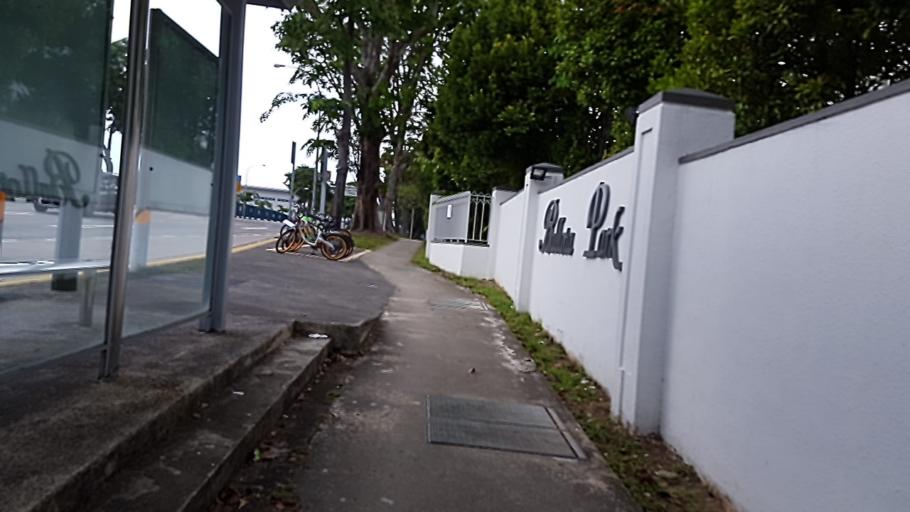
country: SG
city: Singapore
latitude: 1.3580
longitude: 103.9694
